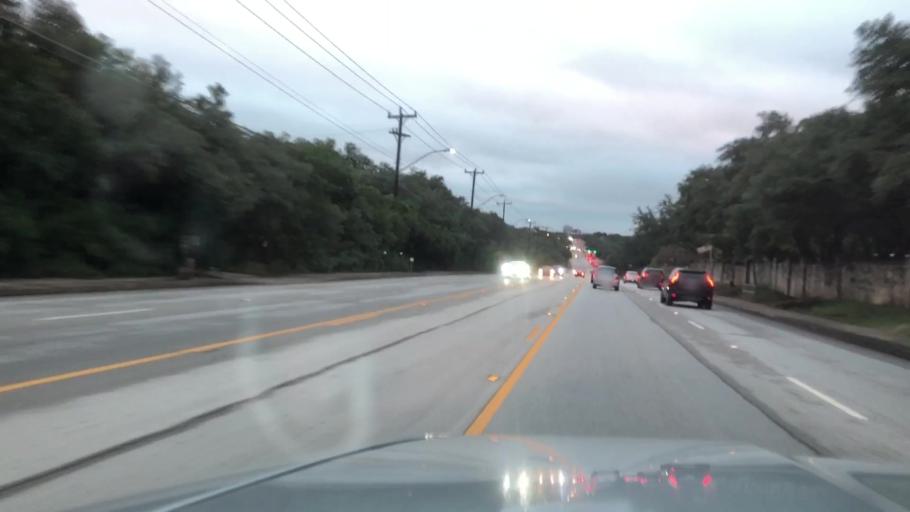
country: US
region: Texas
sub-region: Bexar County
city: Leon Valley
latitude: 29.5381
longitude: -98.6094
